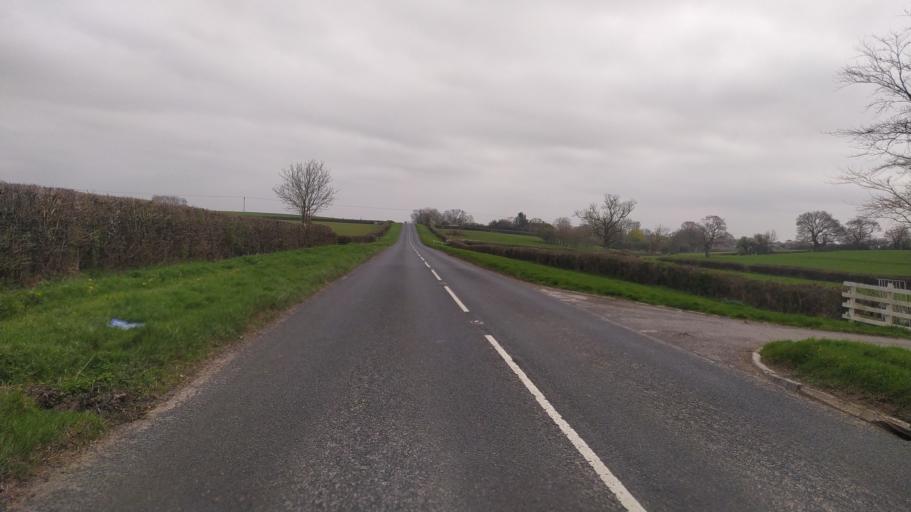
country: GB
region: England
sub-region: Wiltshire
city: Wingfield
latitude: 51.3143
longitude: -2.2444
